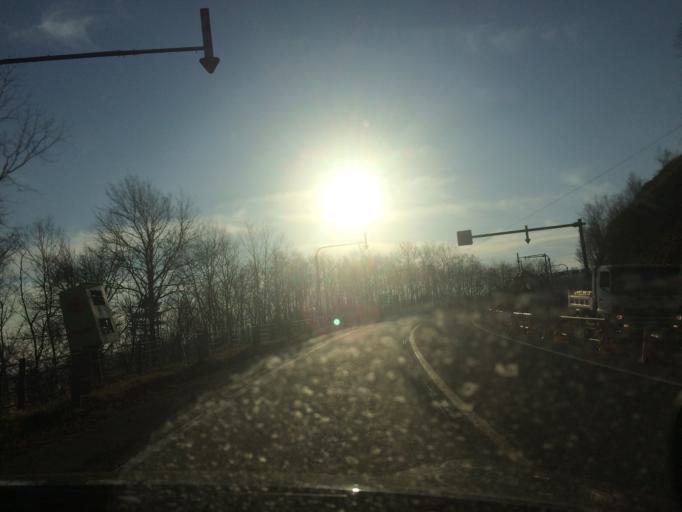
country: JP
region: Hokkaido
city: Otofuke
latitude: 42.9745
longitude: 142.8010
